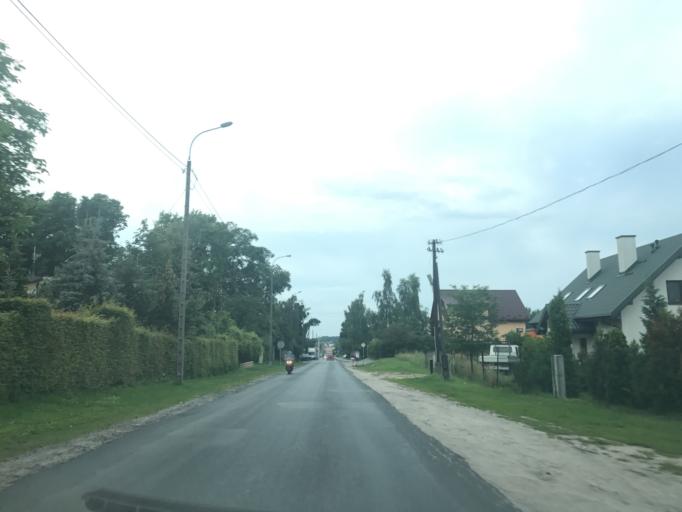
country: PL
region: Kujawsko-Pomorskie
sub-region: Powiat lipnowski
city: Lipno
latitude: 52.8364
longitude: 19.1837
